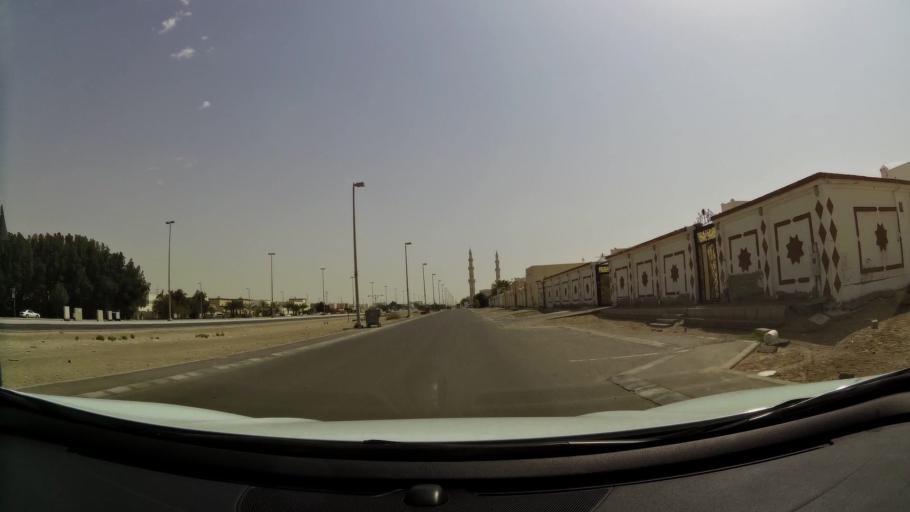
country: AE
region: Abu Dhabi
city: Abu Dhabi
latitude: 24.3027
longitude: 54.6439
